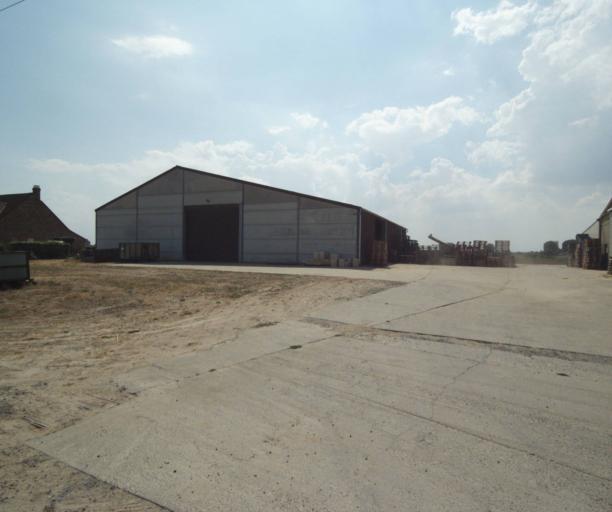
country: FR
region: Nord-Pas-de-Calais
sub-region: Departement du Nord
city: Comines
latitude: 50.7414
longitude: 2.9904
